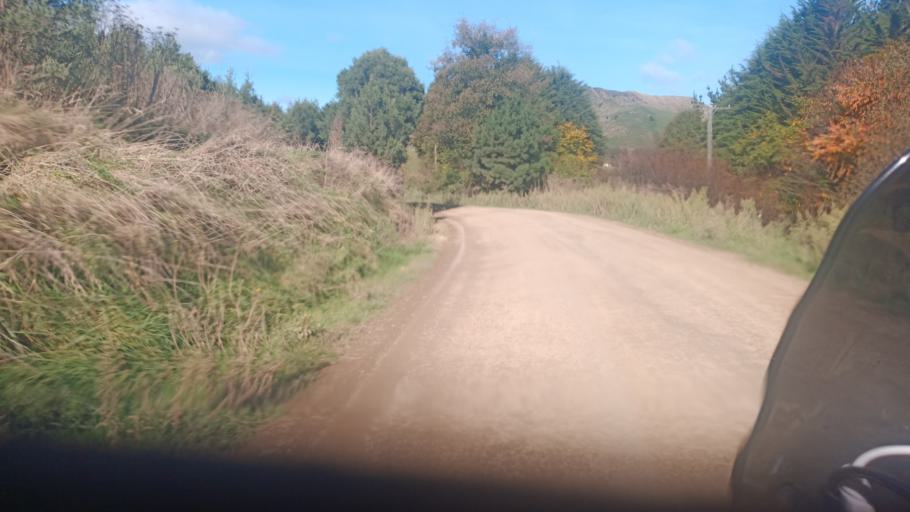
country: NZ
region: Bay of Plenty
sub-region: Opotiki District
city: Opotiki
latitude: -38.4206
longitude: 177.5581
